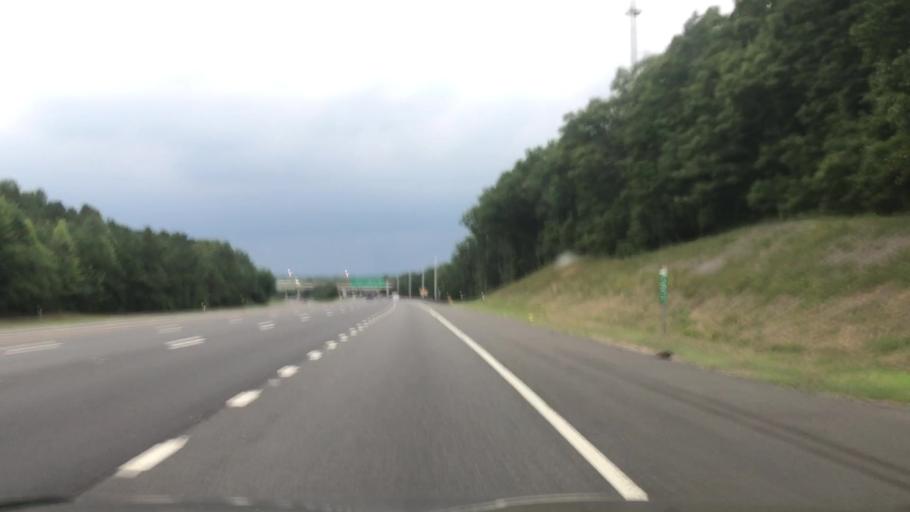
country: US
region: New Jersey
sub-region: Monmouth County
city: Eatontown
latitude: 40.2750
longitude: -74.0797
